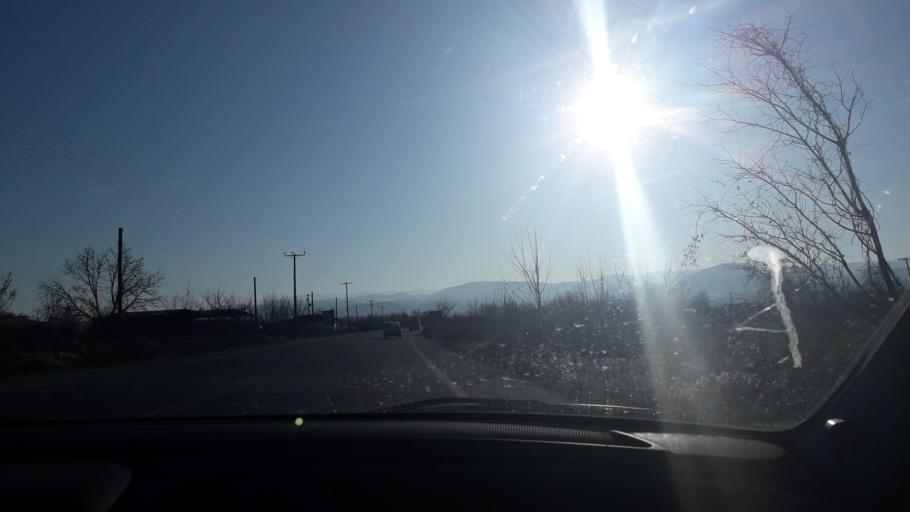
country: GR
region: Central Macedonia
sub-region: Nomos Pellis
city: Apsalos
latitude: 40.9260
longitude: 22.0831
